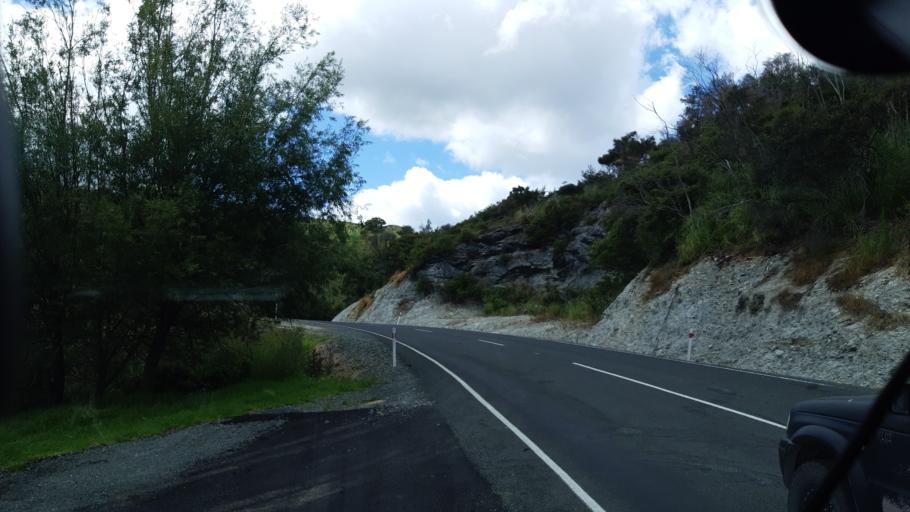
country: NZ
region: Northland
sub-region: Far North District
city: Taipa
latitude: -35.2436
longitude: 173.5344
